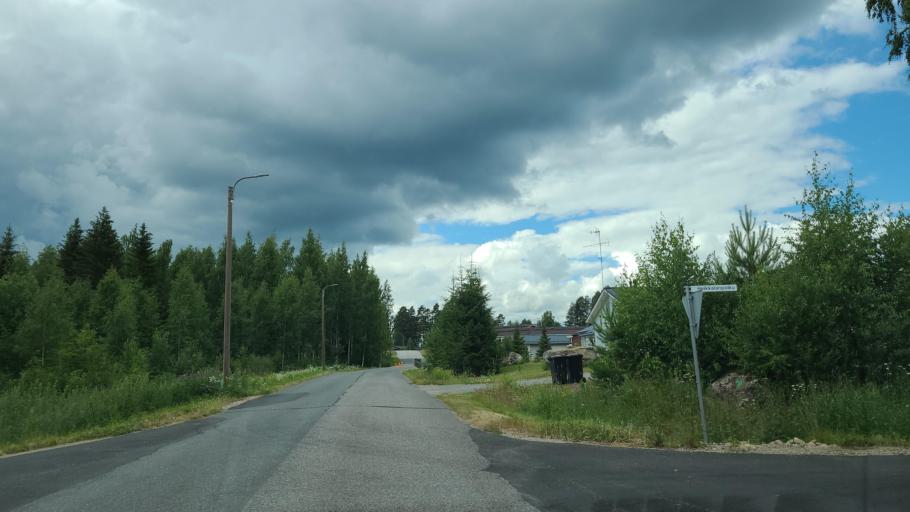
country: FI
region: Northern Savo
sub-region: Koillis-Savo
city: Kaavi
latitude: 62.9728
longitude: 28.4785
